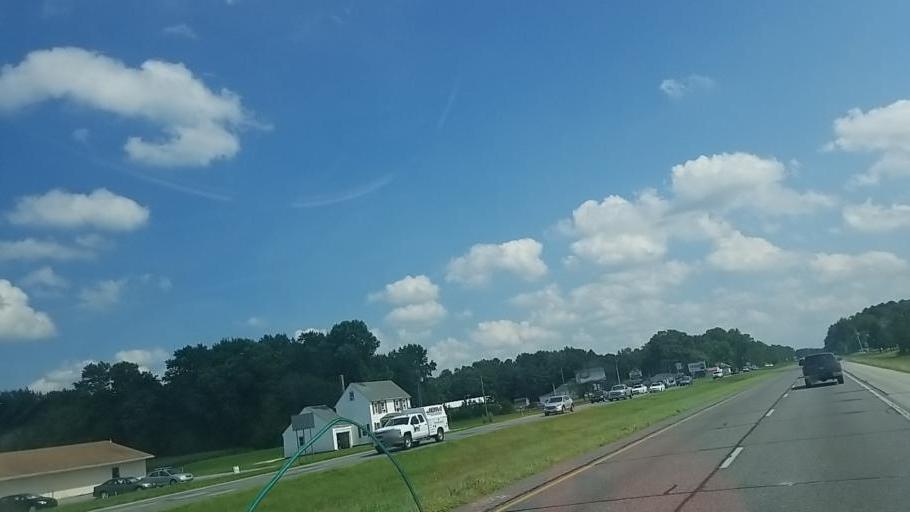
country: US
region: Delaware
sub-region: Sussex County
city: Georgetown
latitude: 38.7378
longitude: -75.4231
